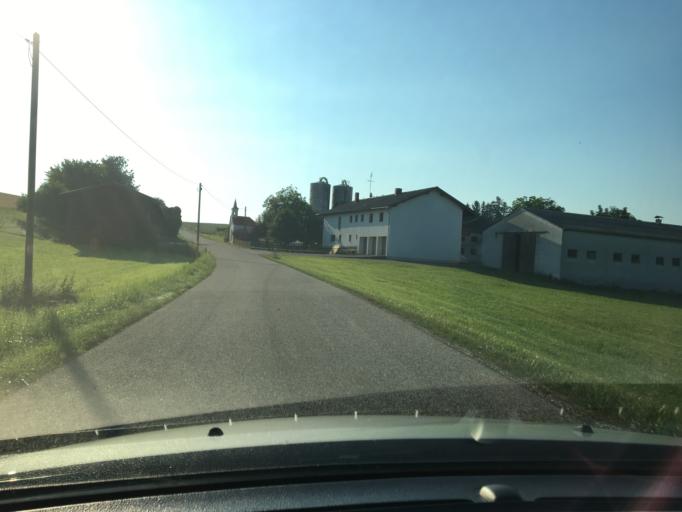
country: DE
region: Bavaria
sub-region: Lower Bavaria
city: Geisenhausen
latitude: 48.4498
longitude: 12.2868
